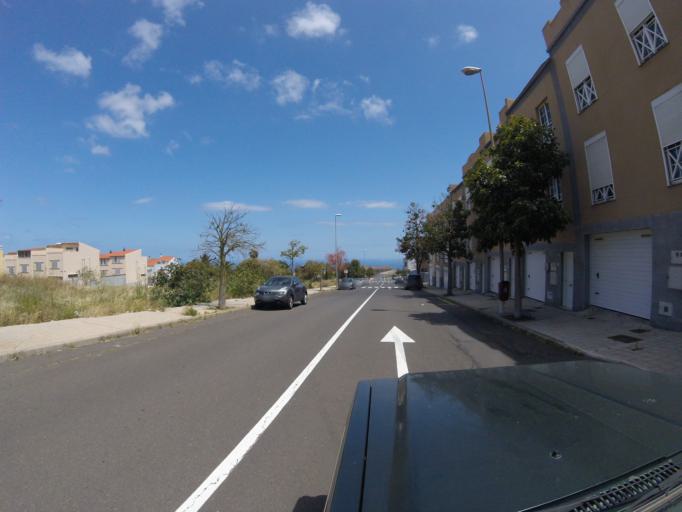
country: ES
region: Canary Islands
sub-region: Provincia de Santa Cruz de Tenerife
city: La Laguna
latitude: 28.4455
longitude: -16.3137
